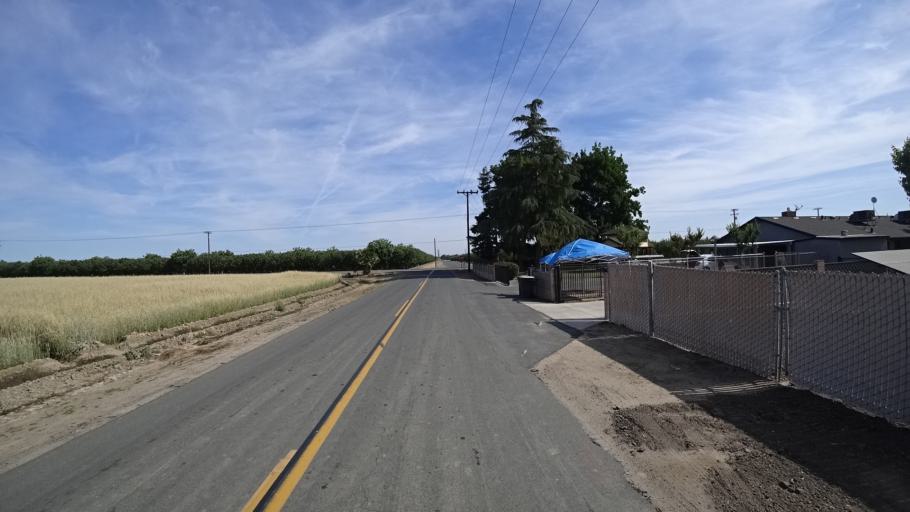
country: US
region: California
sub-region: Kings County
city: Lucerne
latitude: 36.3710
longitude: -119.6100
